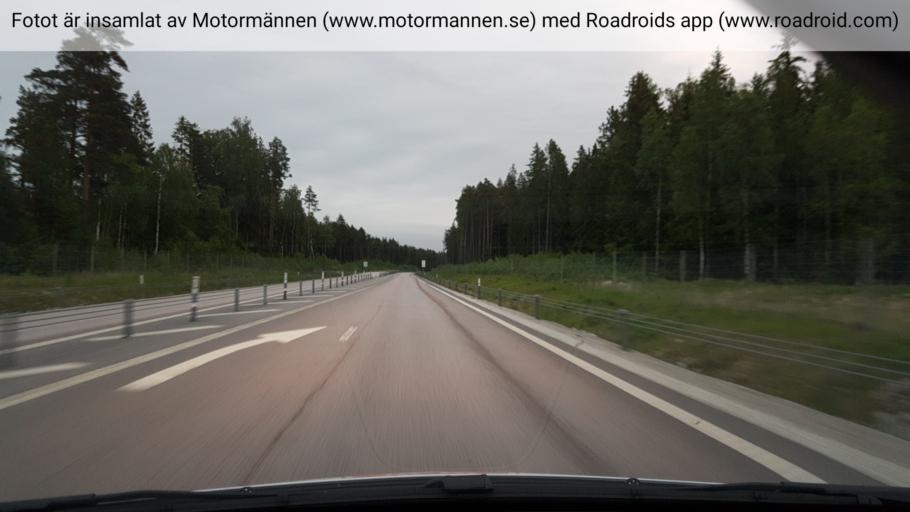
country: SE
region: Vaestmanland
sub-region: Sala Kommun
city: Sala
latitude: 59.8866
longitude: 16.5939
